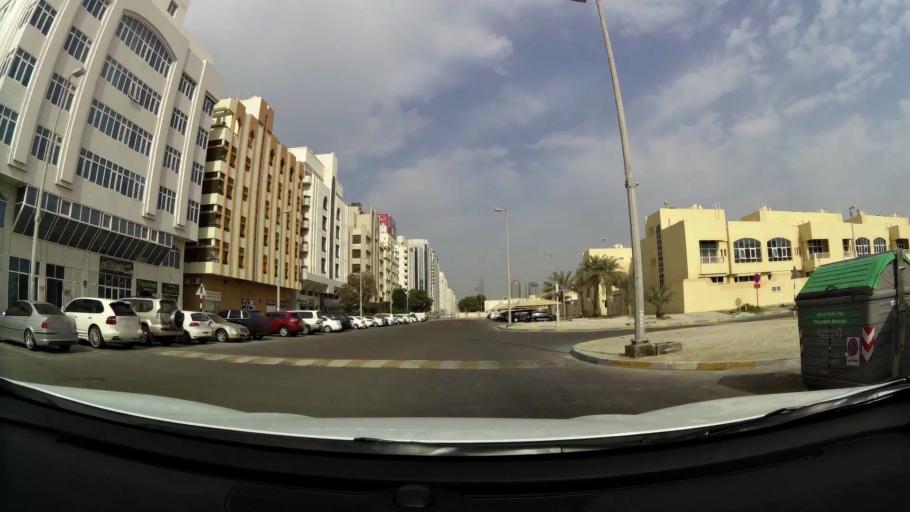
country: AE
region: Abu Dhabi
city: Abu Dhabi
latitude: 24.4571
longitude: 54.3843
